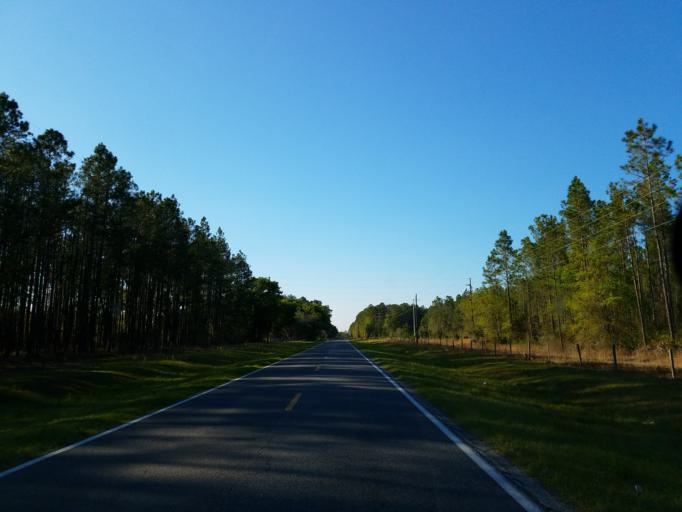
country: US
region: Florida
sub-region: Suwannee County
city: Wellborn
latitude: 30.2007
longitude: -82.9149
